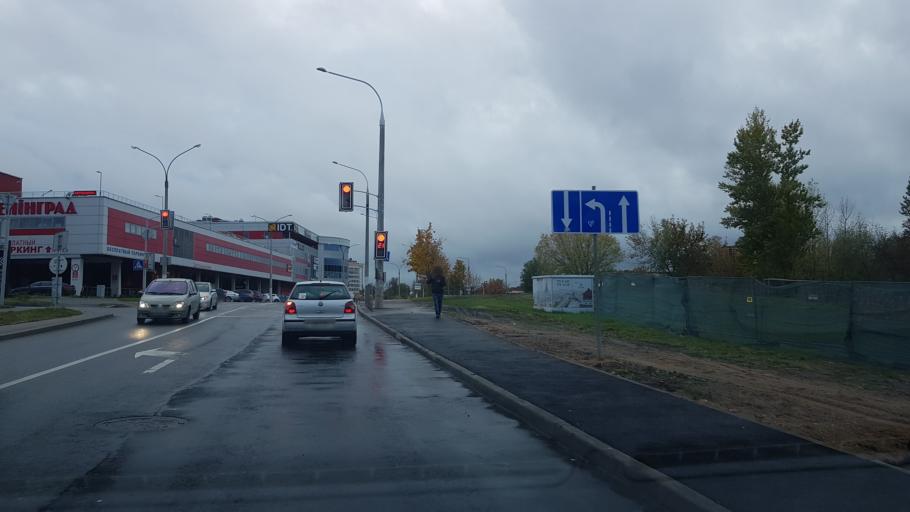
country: BY
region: Minsk
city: Minsk
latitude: 53.8902
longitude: 27.5825
